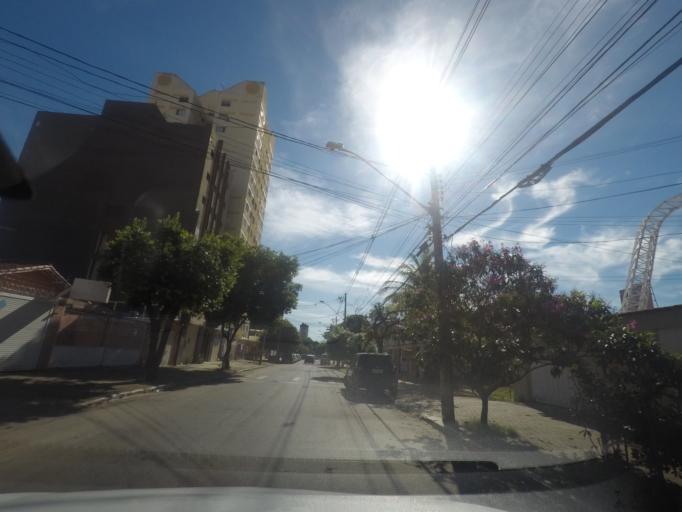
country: BR
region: Goias
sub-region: Goiania
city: Goiania
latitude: -16.6694
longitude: -49.2631
